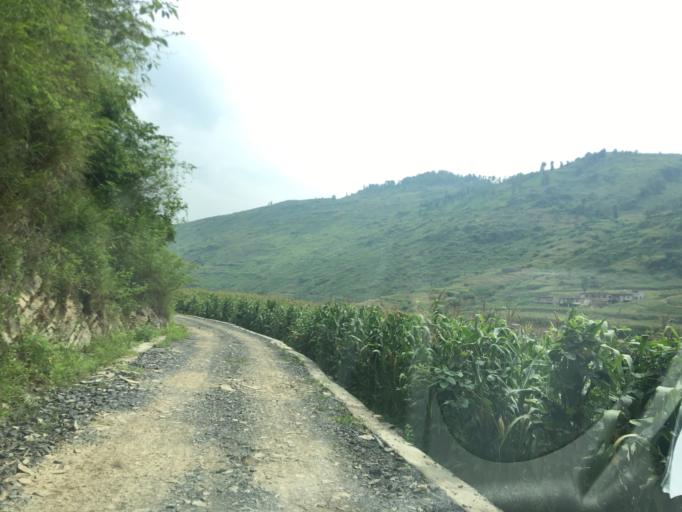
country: CN
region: Guangxi Zhuangzu Zizhiqu
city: Xinzhou
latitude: 25.1943
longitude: 105.7330
